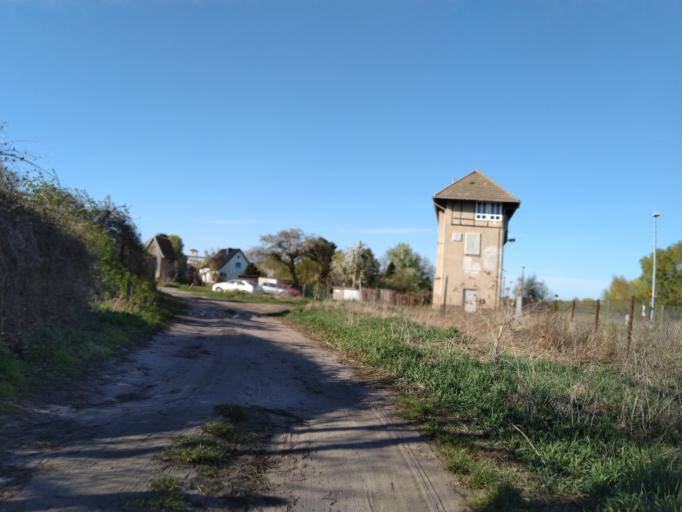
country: DE
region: Brandenburg
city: Wriezen
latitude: 52.7102
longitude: 14.1370
